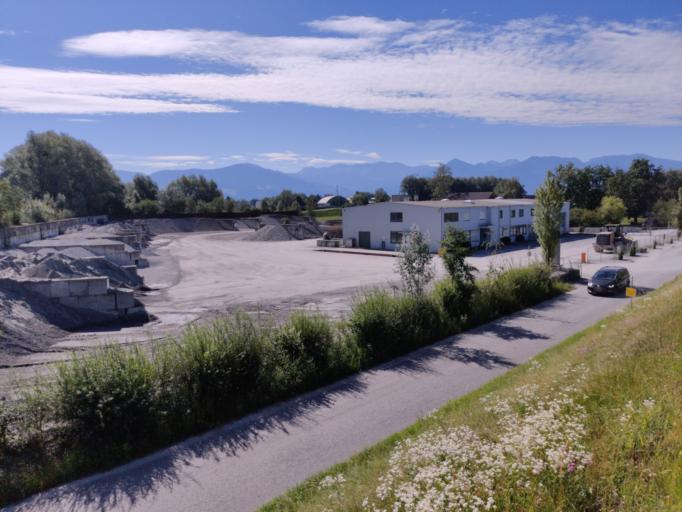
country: AT
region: Vorarlberg
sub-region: Politischer Bezirk Bregenz
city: Fussach
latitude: 47.4798
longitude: 9.6713
